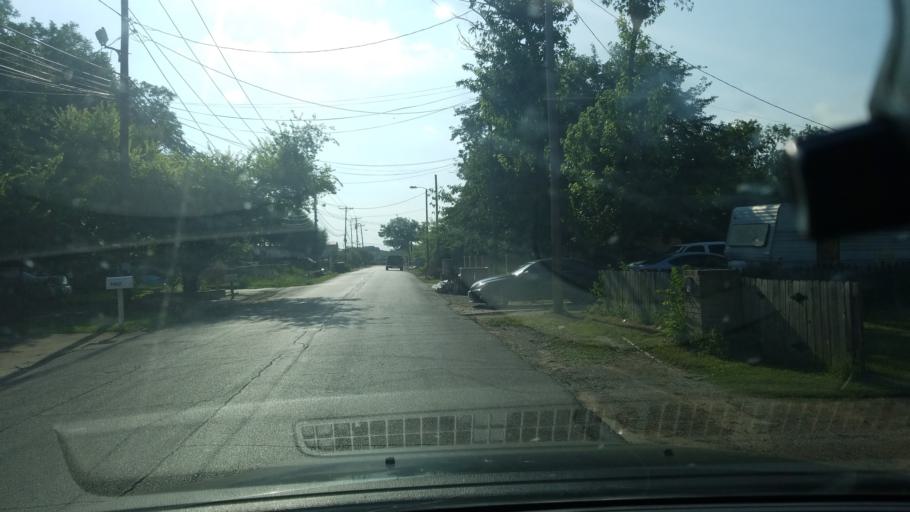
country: US
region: Texas
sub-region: Dallas County
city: Balch Springs
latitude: 32.7252
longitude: -96.6854
